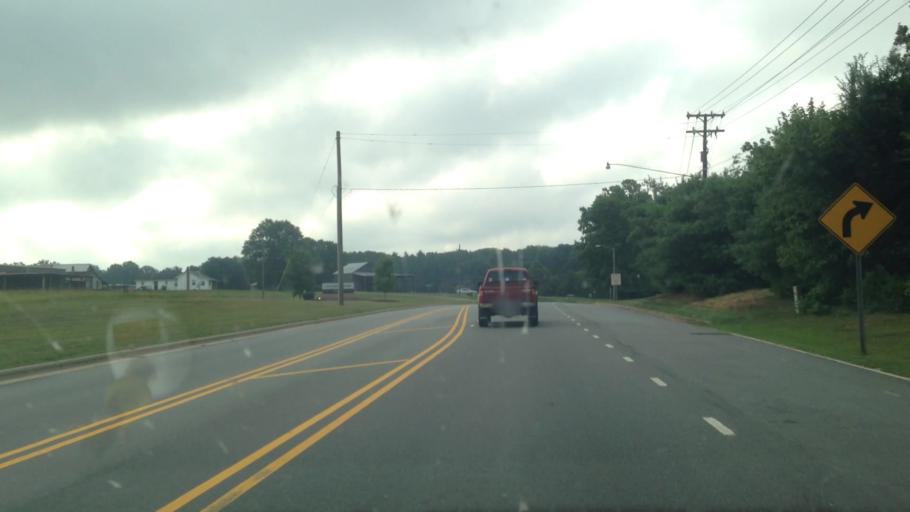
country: US
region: North Carolina
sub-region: Forsyth County
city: Kernersville
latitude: 36.1312
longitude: -80.0881
